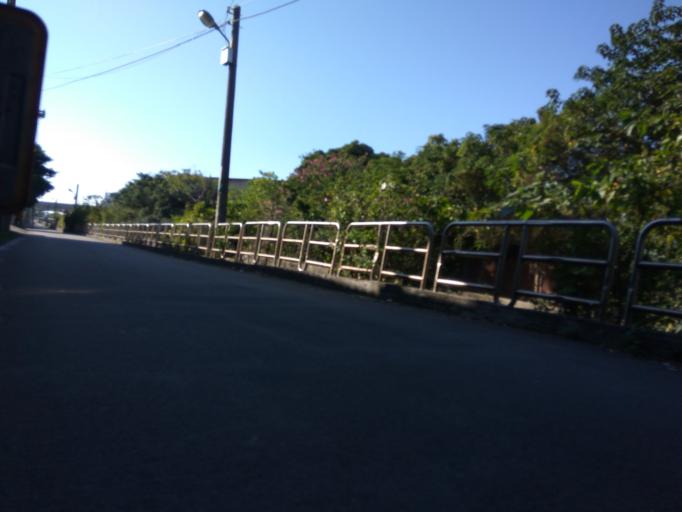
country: TW
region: Taiwan
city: Taoyuan City
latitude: 24.9837
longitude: 121.1881
